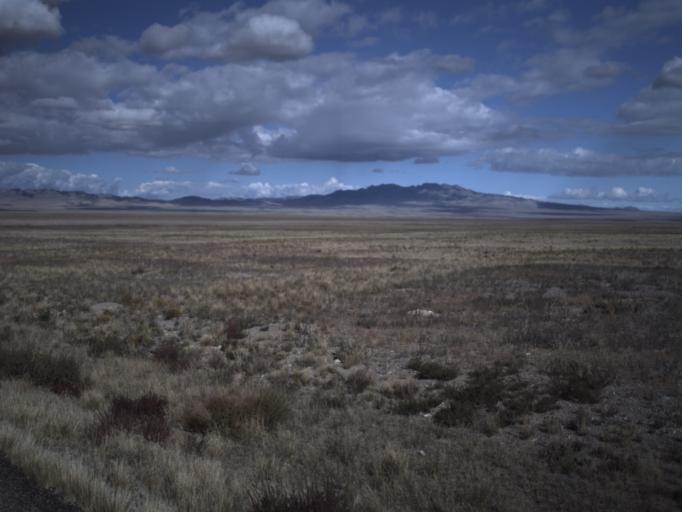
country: US
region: Utah
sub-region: Beaver County
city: Milford
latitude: 38.5179
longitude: -113.6429
